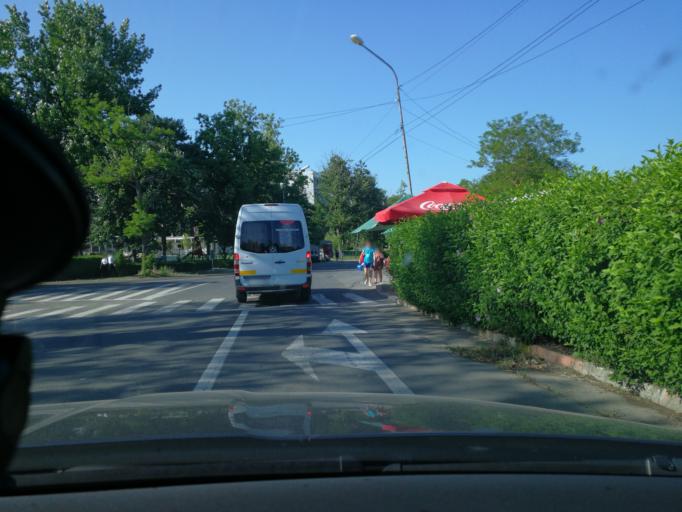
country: RO
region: Constanta
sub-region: Municipiul Mangalia
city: Mangalia
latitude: 43.8484
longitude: 28.5997
